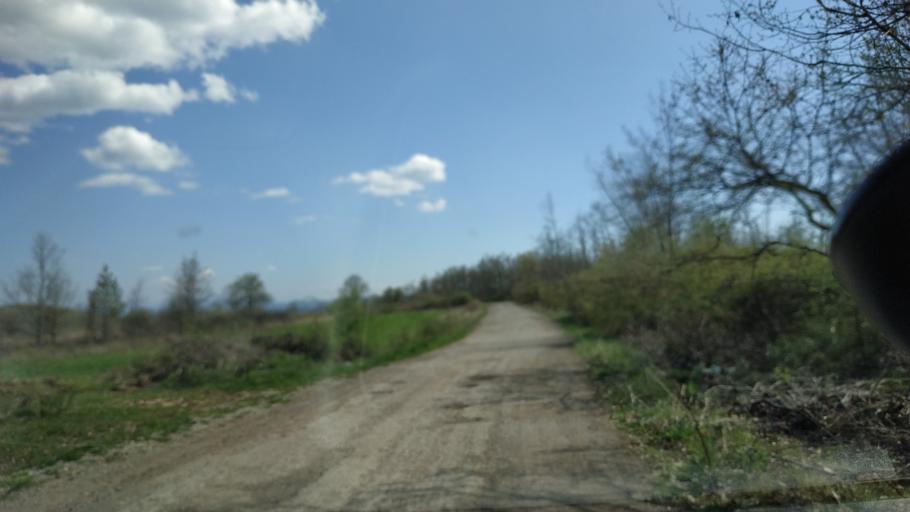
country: RS
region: Central Serbia
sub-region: Zajecarski Okrug
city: Soko Banja
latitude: 43.5471
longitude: 21.9006
